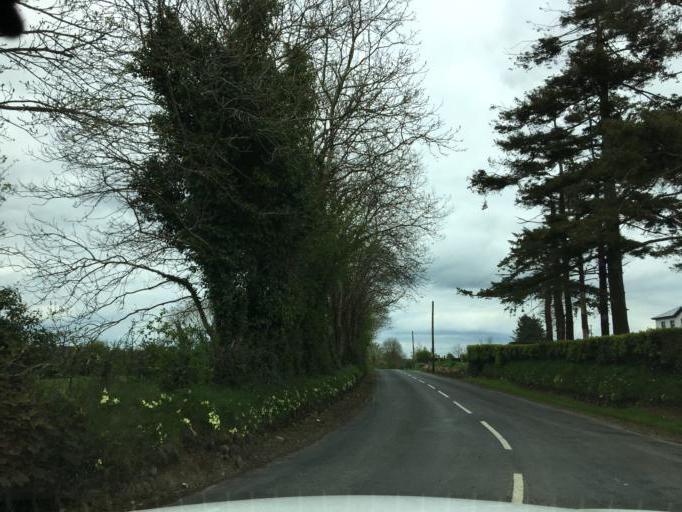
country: IE
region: Leinster
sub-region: Loch Garman
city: New Ross
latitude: 52.4158
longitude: -6.7839
